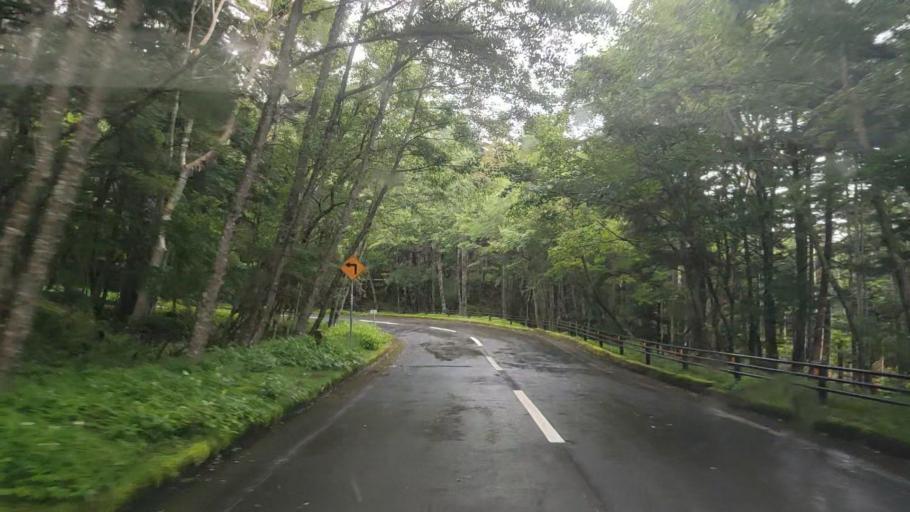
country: JP
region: Shizuoka
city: Fujinomiya
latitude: 35.3251
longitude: 138.7237
